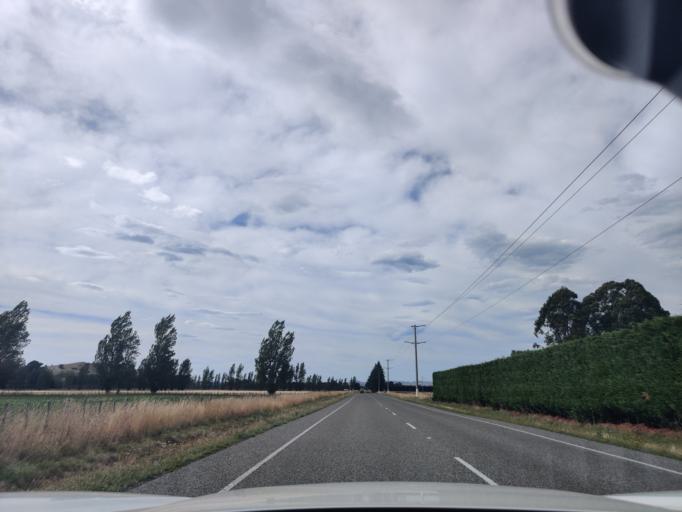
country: NZ
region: Wellington
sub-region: Masterton District
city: Masterton
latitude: -40.8498
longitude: 175.6356
